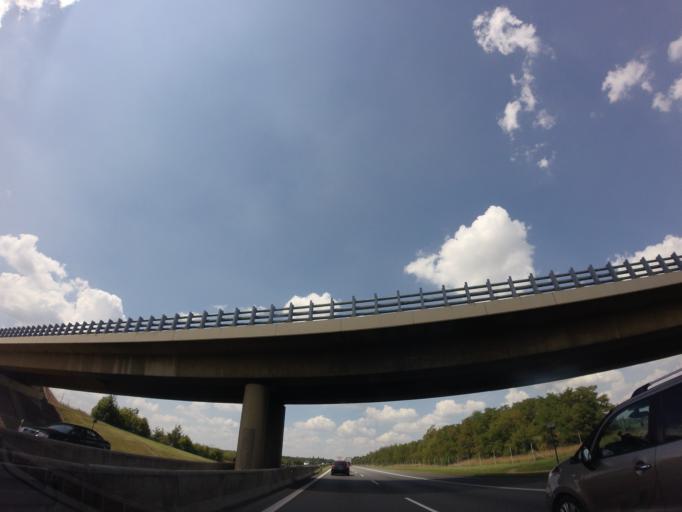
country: PL
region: Opole Voivodeship
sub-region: Powiat opolski
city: Proszkow
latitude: 50.5771
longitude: 17.8432
